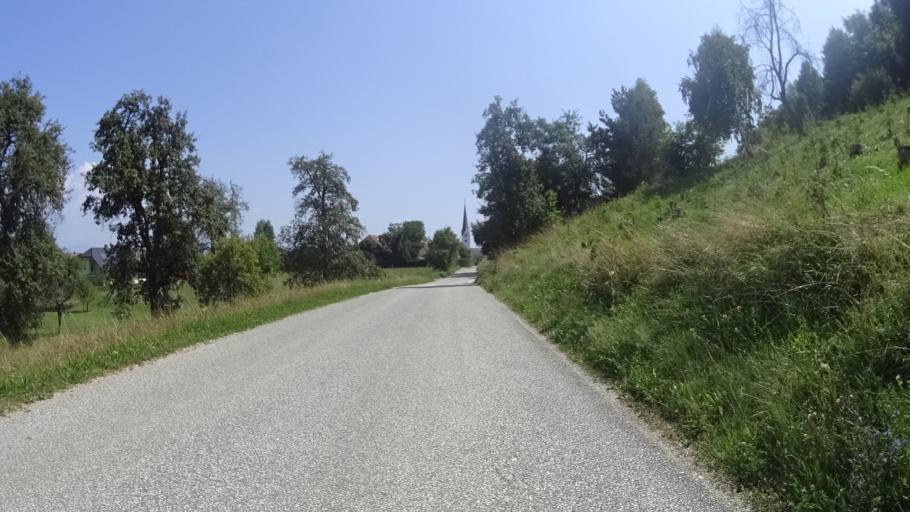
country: AT
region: Carinthia
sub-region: Politischer Bezirk Volkermarkt
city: Globasnitz
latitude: 46.5572
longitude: 14.6975
